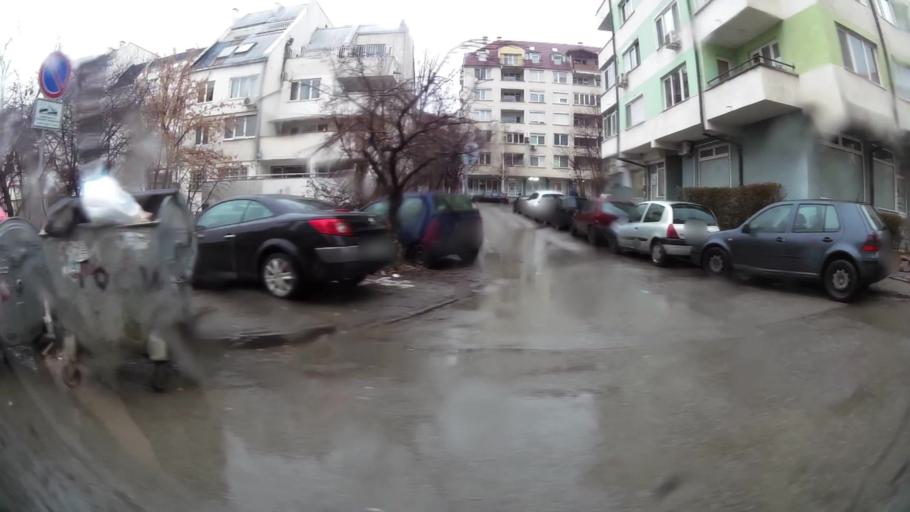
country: BG
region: Sofia-Capital
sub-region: Stolichna Obshtina
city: Sofia
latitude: 42.6573
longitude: 23.3752
